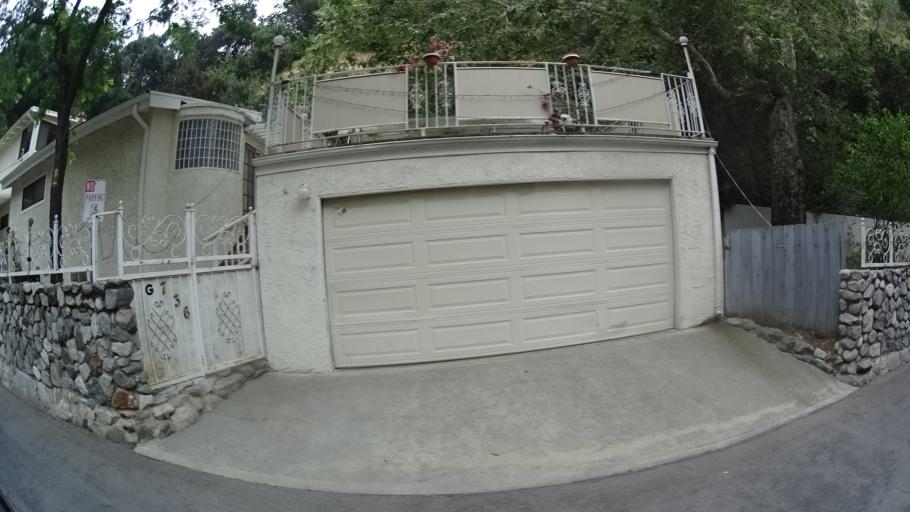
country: US
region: California
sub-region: Los Angeles County
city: Burbank
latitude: 34.1992
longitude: -118.2931
